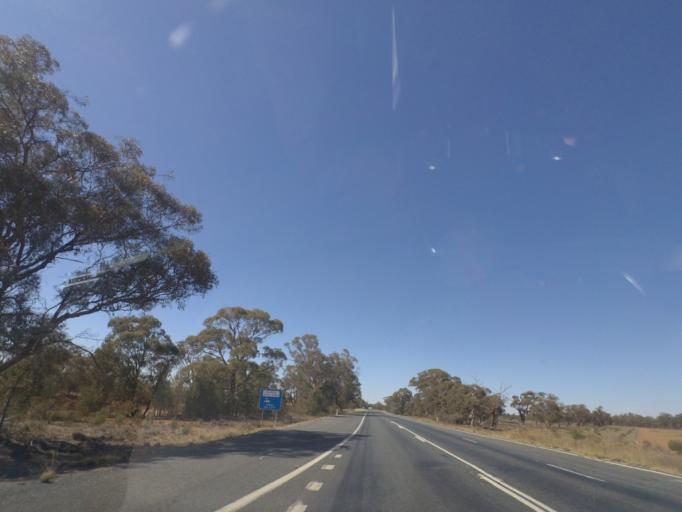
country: AU
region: New South Wales
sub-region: Bland
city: West Wyalong
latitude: -34.1938
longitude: 147.1112
